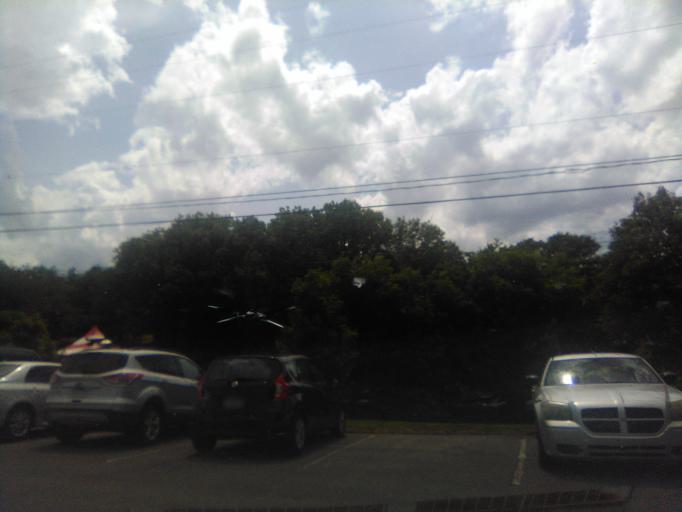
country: US
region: Tennessee
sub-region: Davidson County
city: Belle Meade
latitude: 36.0858
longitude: -86.8903
